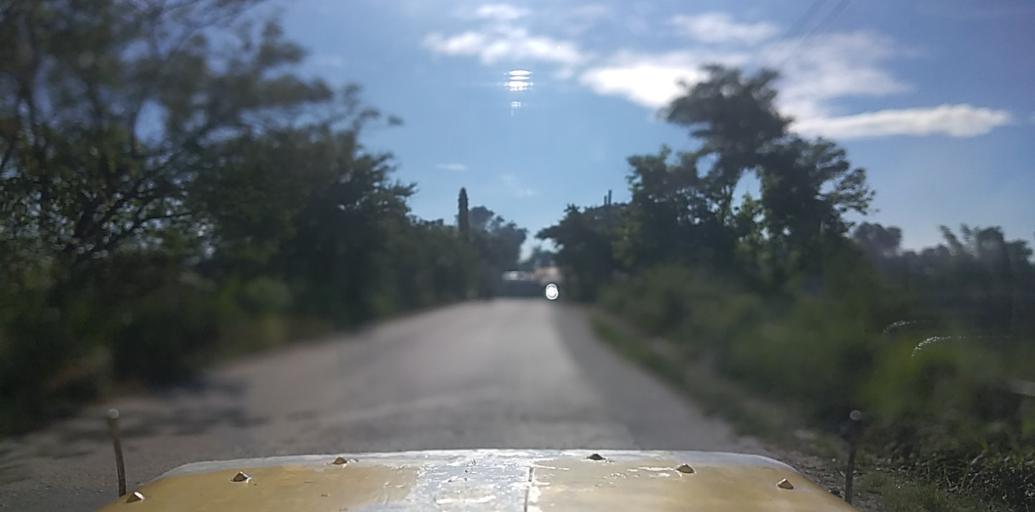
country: PH
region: Central Luzon
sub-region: Province of Pampanga
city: Anao
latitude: 15.1195
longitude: 120.7024
